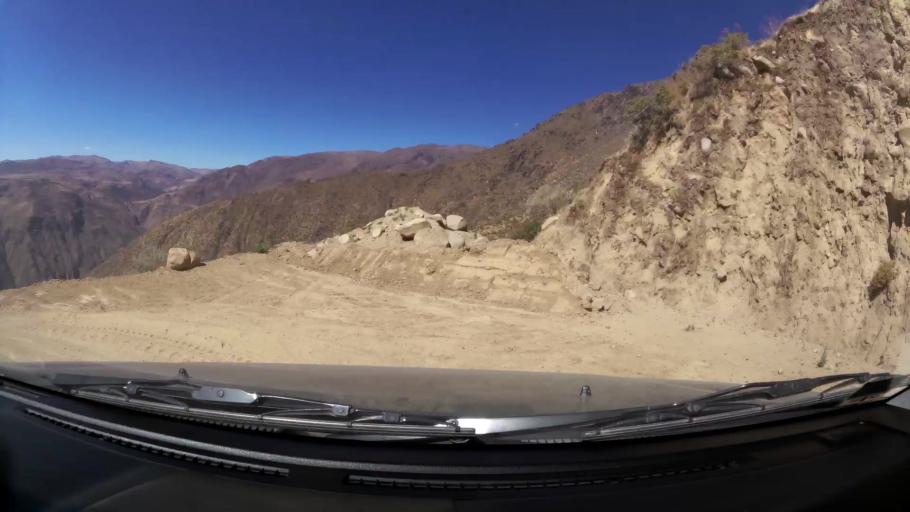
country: PE
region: Huancavelica
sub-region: Huaytara
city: Quito-Arma
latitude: -13.6200
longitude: -75.3517
